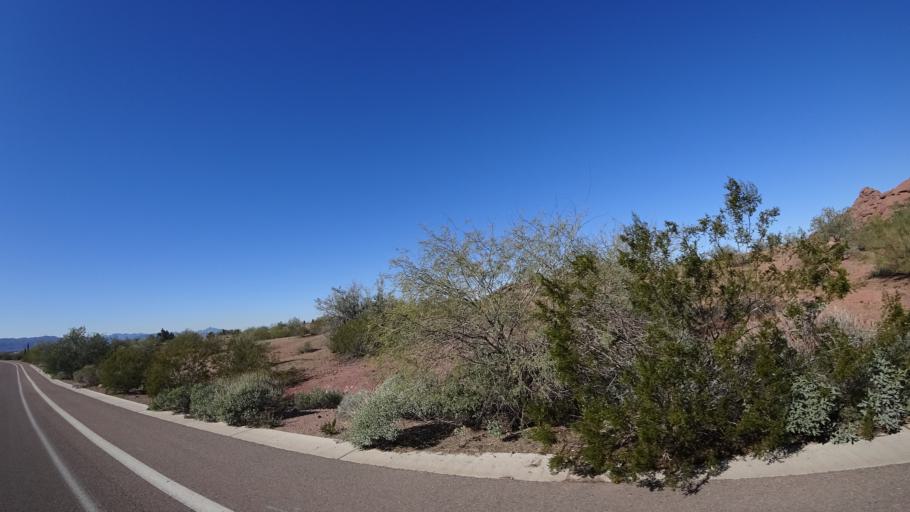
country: US
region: Arizona
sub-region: Maricopa County
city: Tempe Junction
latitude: 33.4592
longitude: -111.9502
